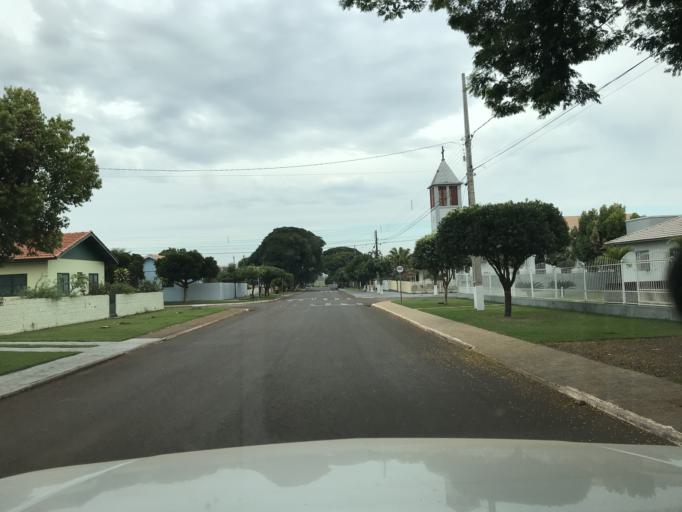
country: BR
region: Parana
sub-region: Marechal Candido Rondon
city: Marechal Candido Rondon
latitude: -24.4668
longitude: -53.9572
